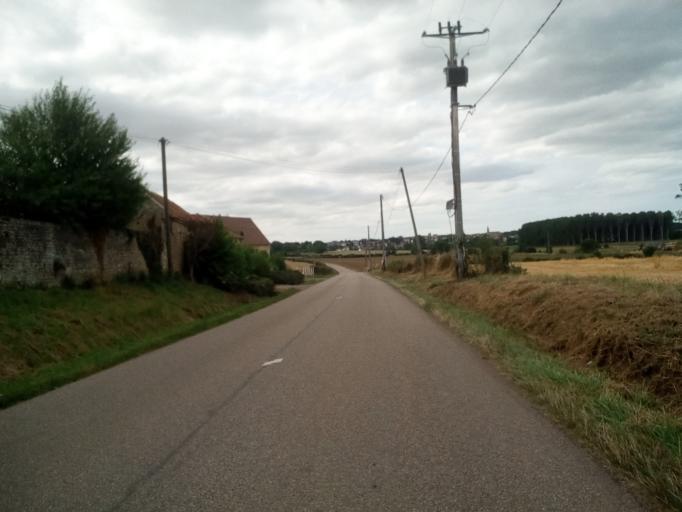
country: FR
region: Lower Normandy
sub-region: Departement du Calvados
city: Troarn
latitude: 49.1716
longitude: -0.1647
